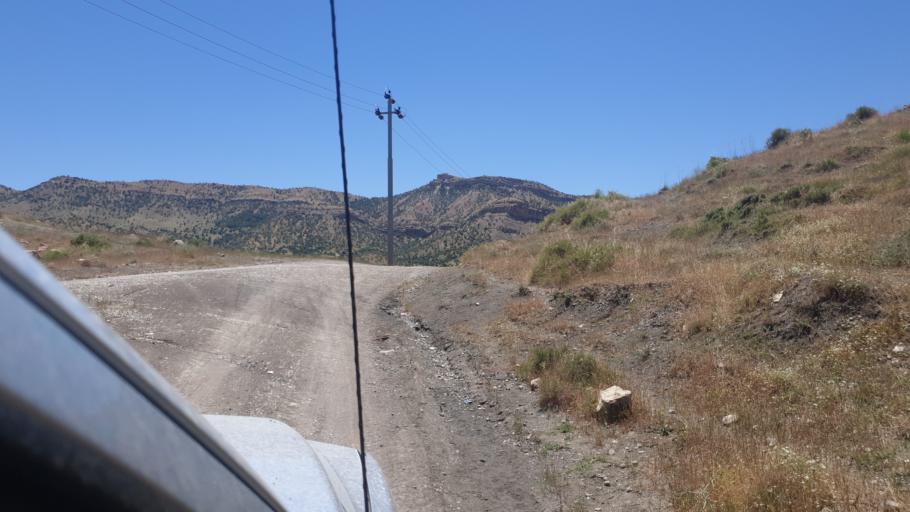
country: IQ
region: Arbil
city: Nahiyat Hiran
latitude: 36.2002
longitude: 44.4227
